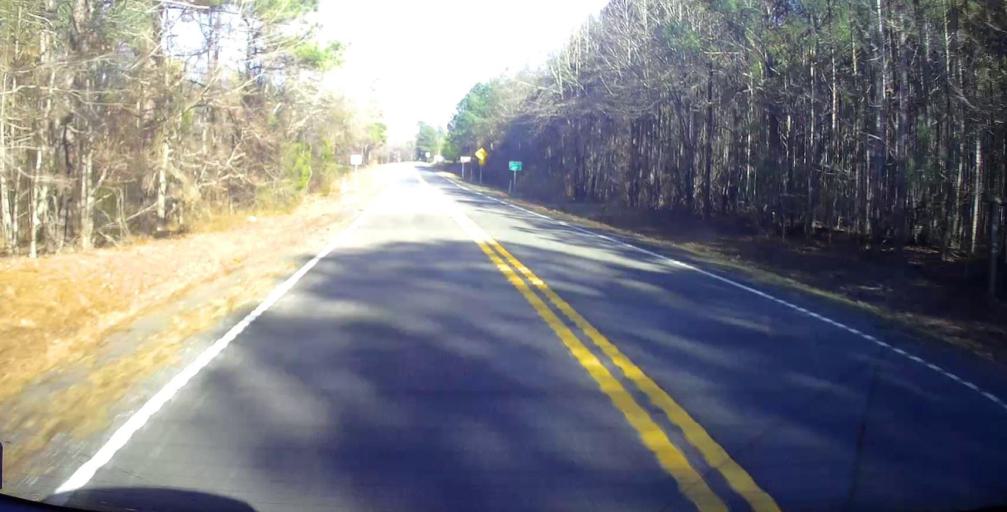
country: US
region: Georgia
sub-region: Taylor County
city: Butler
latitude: 32.6466
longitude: -84.3745
